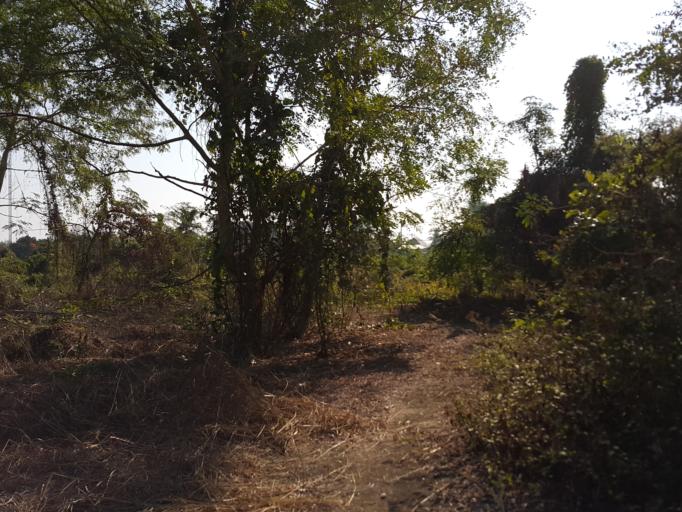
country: TH
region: Chiang Mai
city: San Kamphaeng
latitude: 18.8067
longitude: 99.1139
